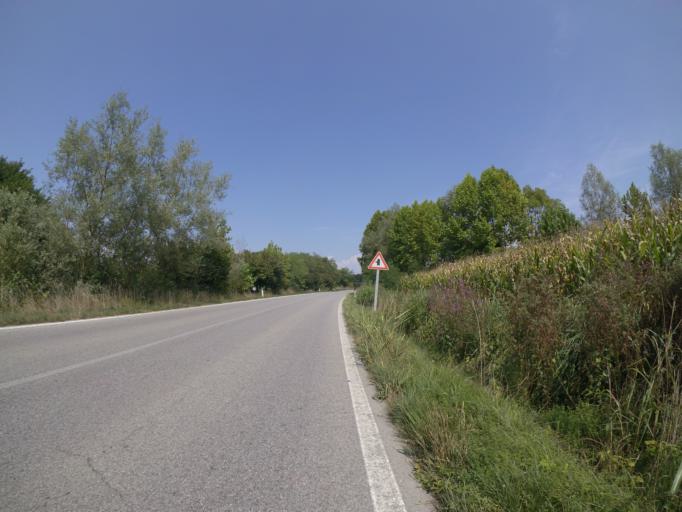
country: IT
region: Friuli Venezia Giulia
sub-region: Provincia di Udine
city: Pocenia
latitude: 45.8424
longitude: 13.0976
